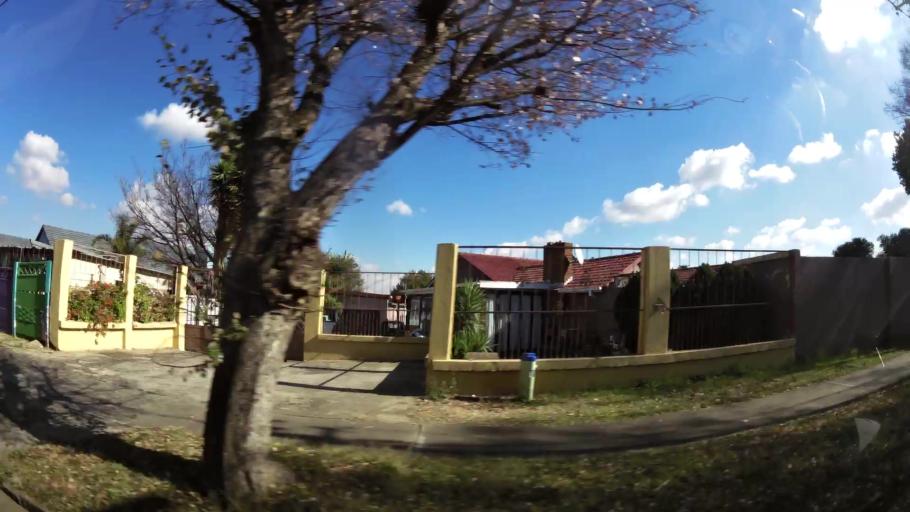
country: ZA
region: Gauteng
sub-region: City of Johannesburg Metropolitan Municipality
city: Roodepoort
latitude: -26.1371
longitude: 27.8295
